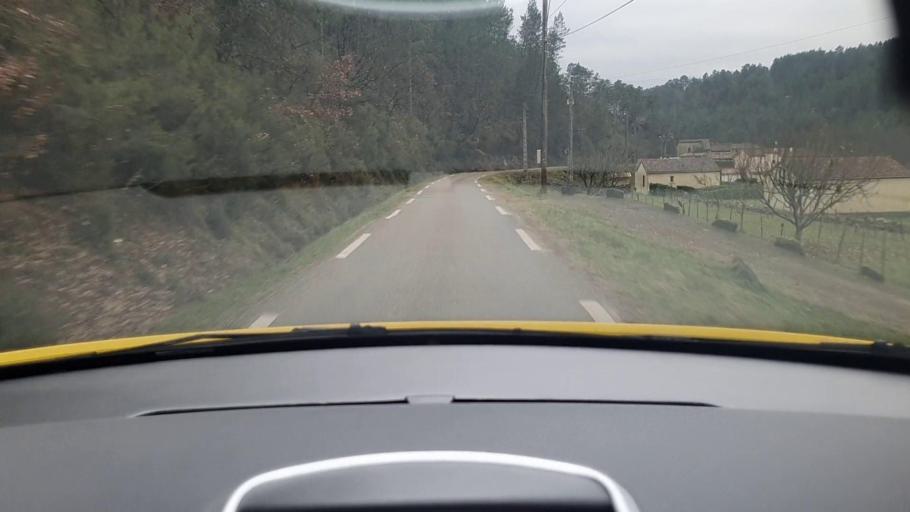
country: FR
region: Languedoc-Roussillon
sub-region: Departement du Gard
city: Besseges
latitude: 44.3259
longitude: 4.1195
